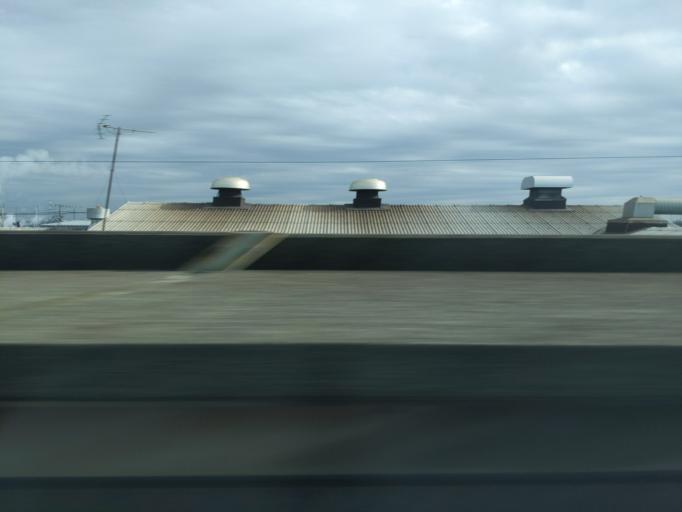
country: JP
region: Saitama
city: Kukichuo
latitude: 36.0838
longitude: 139.6890
